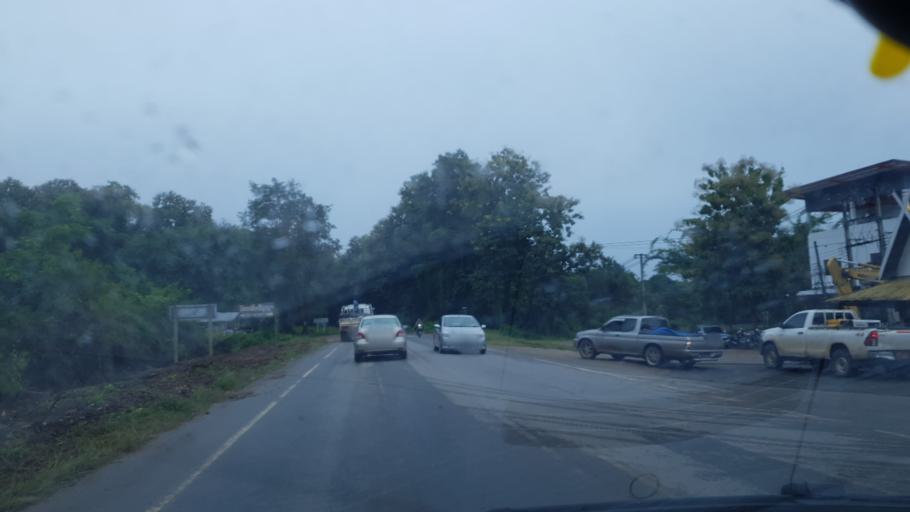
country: TH
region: Mae Hong Son
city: Pa Pae
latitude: 18.1895
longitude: 97.9360
